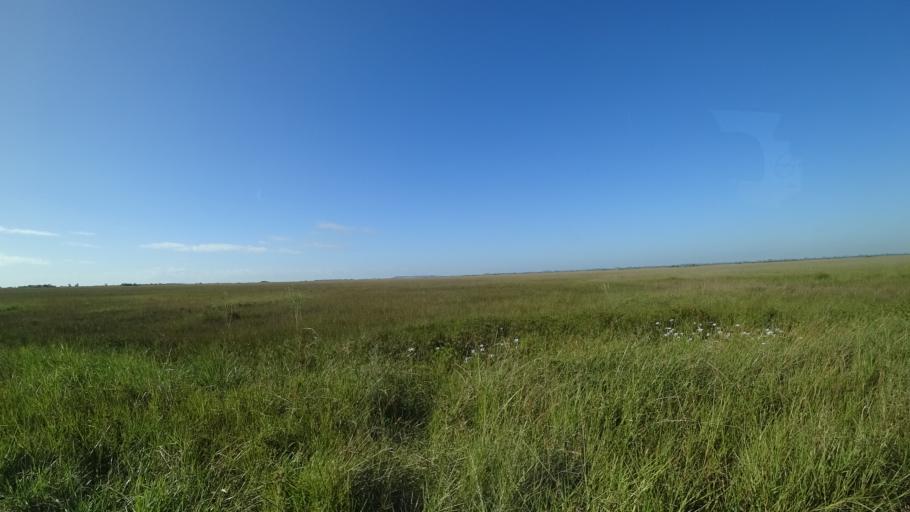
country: MZ
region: Sofala
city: Beira
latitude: -19.7521
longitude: 34.9339
